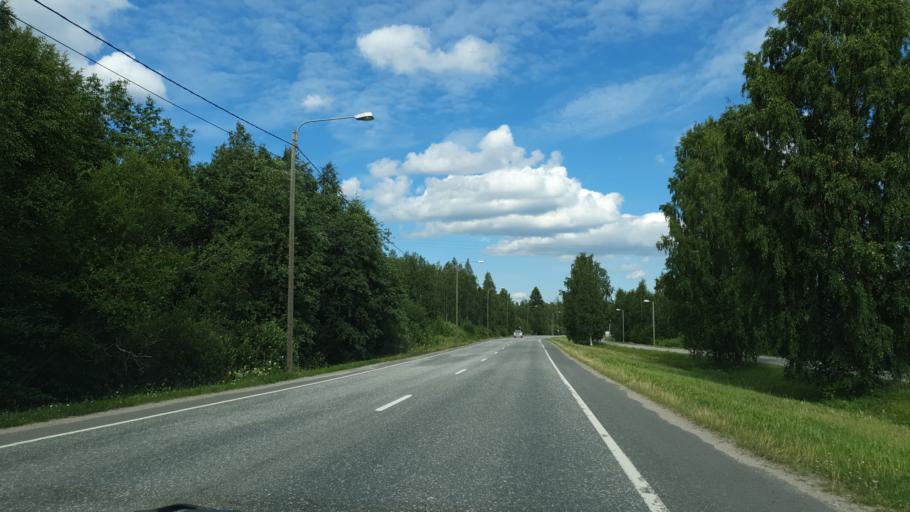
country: FI
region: Kainuu
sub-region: Kajaani
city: Kajaani
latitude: 64.2459
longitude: 27.7636
